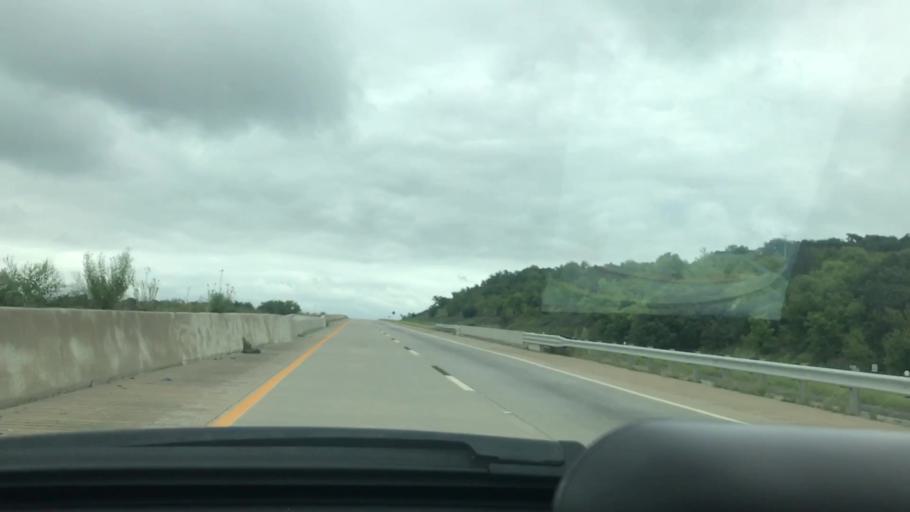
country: US
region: Oklahoma
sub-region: McIntosh County
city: Eufaula
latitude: 35.1716
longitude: -95.6493
